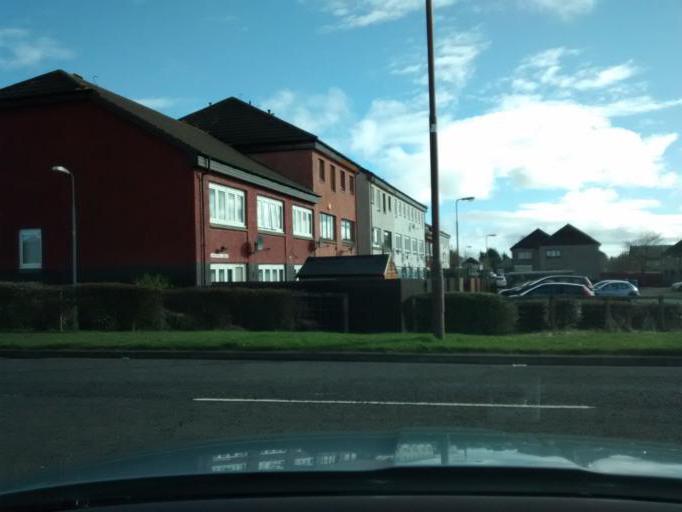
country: GB
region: Scotland
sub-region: West Lothian
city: Mid Calder
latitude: 55.8953
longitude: -3.4929
